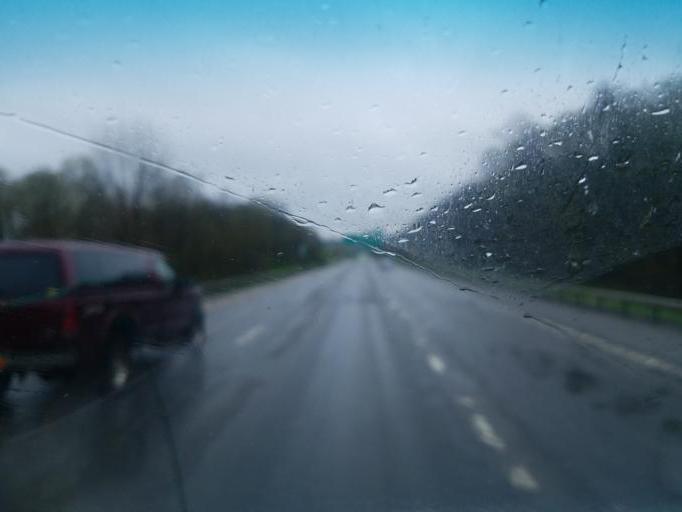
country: US
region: New York
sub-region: Chautauqua County
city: Lakewood
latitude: 42.1504
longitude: -79.3663
